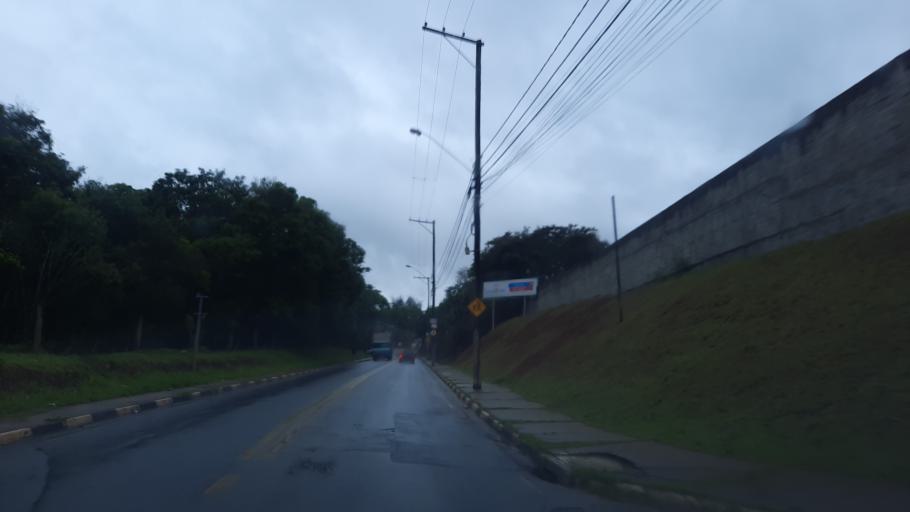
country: BR
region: Sao Paulo
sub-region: Atibaia
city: Atibaia
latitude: -23.0950
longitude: -46.5466
